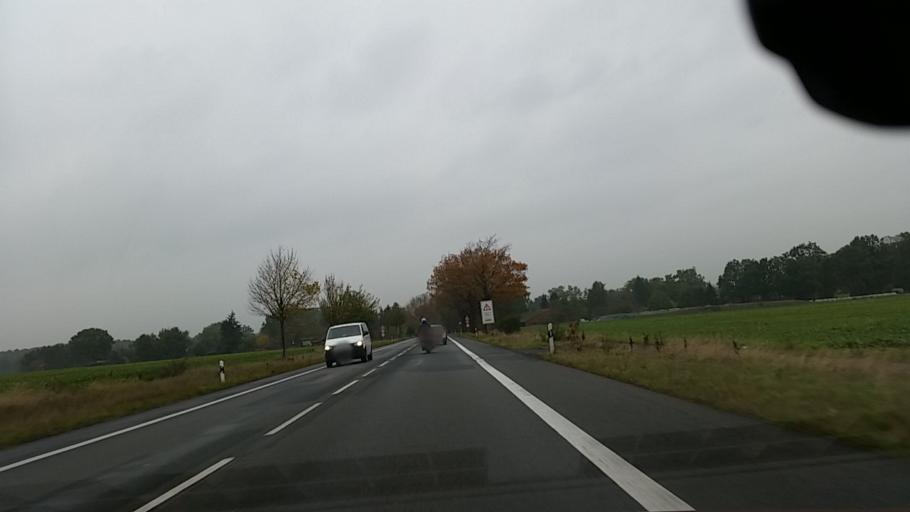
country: DE
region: Lower Saxony
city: Jelmstorf
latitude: 53.0955
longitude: 10.5248
